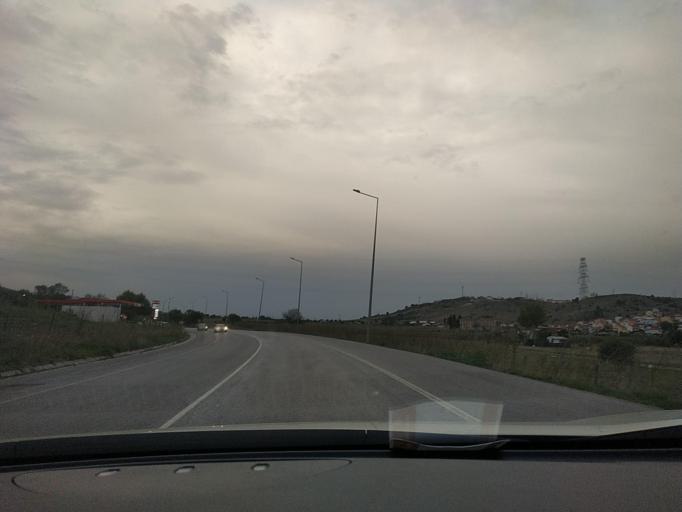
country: PT
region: Lisbon
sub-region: Loures
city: Santa Iria da Azoia
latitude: 38.8630
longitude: -9.1006
